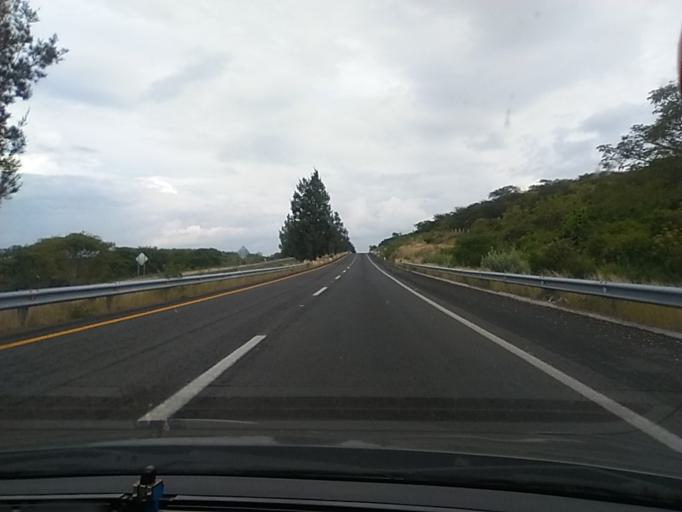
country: MX
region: Michoacan
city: Ixtlan
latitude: 20.2033
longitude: -102.3347
